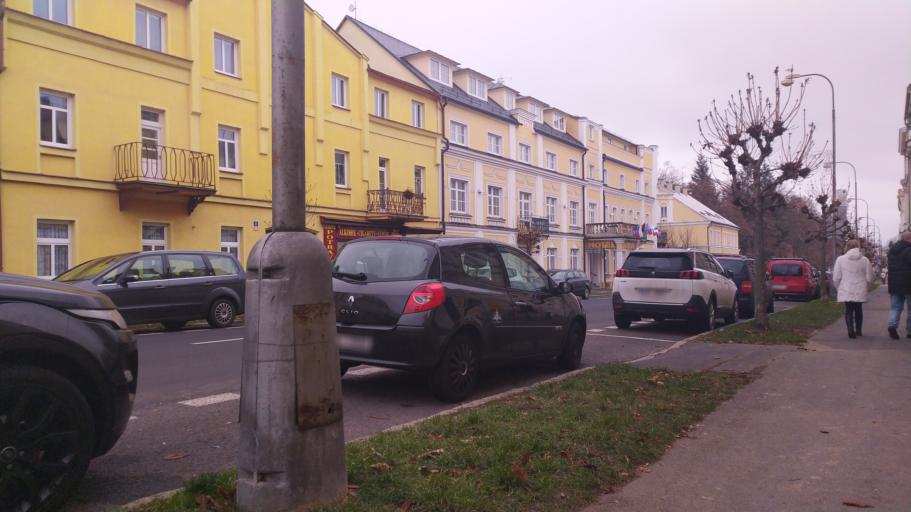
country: CZ
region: Karlovarsky
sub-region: Okres Cheb
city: Frantiskovy Lazne
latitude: 50.1233
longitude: 12.3477
